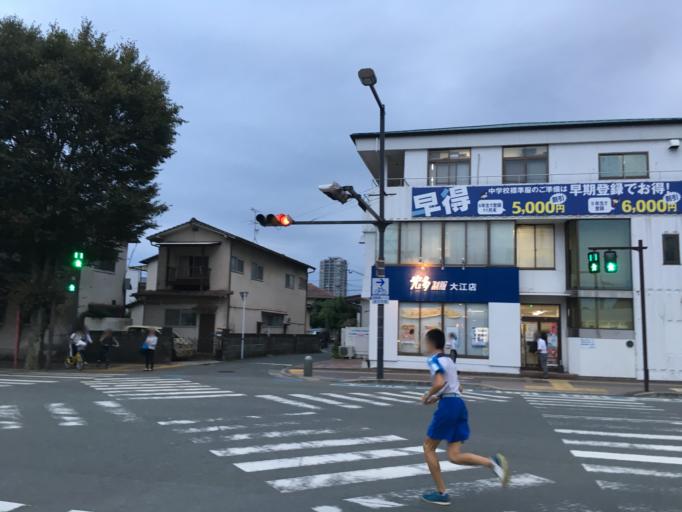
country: JP
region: Kumamoto
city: Kumamoto
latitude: 32.8009
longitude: 130.7275
